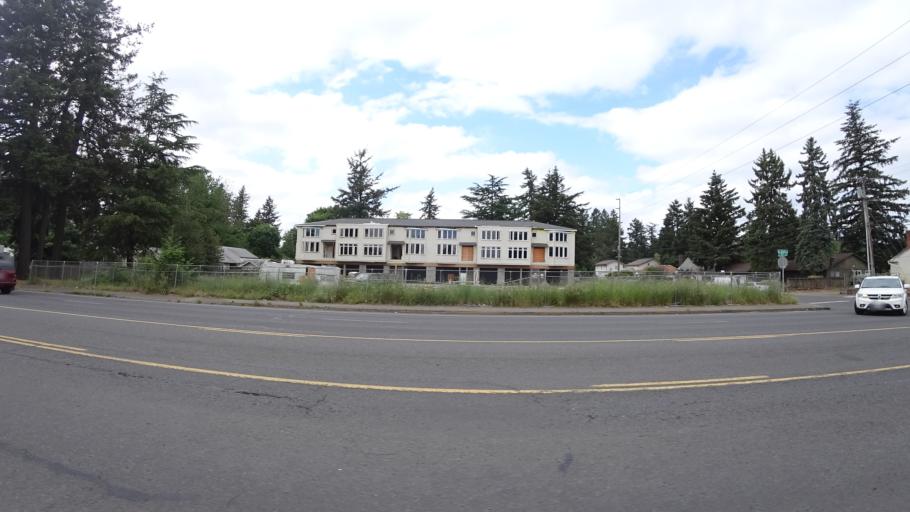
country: US
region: Oregon
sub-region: Multnomah County
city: Fairview
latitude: 45.5191
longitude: -122.4864
